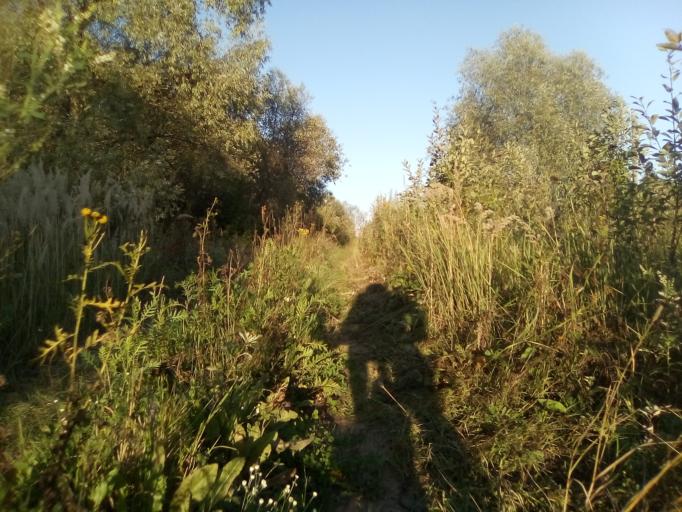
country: RU
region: Moskovskaya
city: Krasnoznamensk
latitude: 55.5812
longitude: 37.0528
